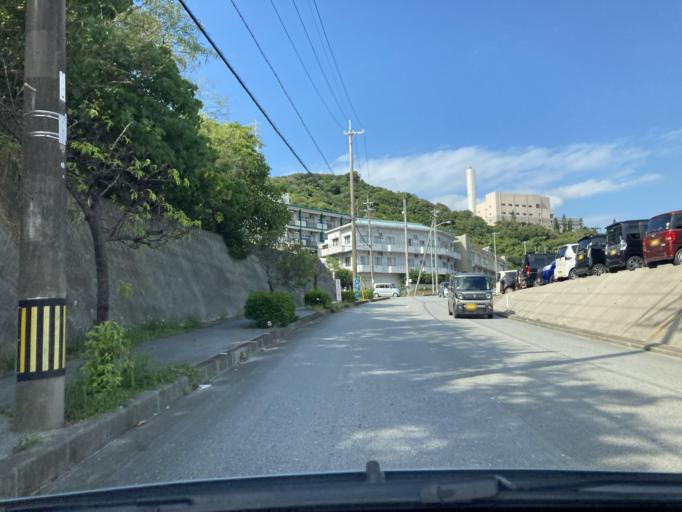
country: JP
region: Okinawa
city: Ginowan
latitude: 26.2759
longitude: 127.7967
